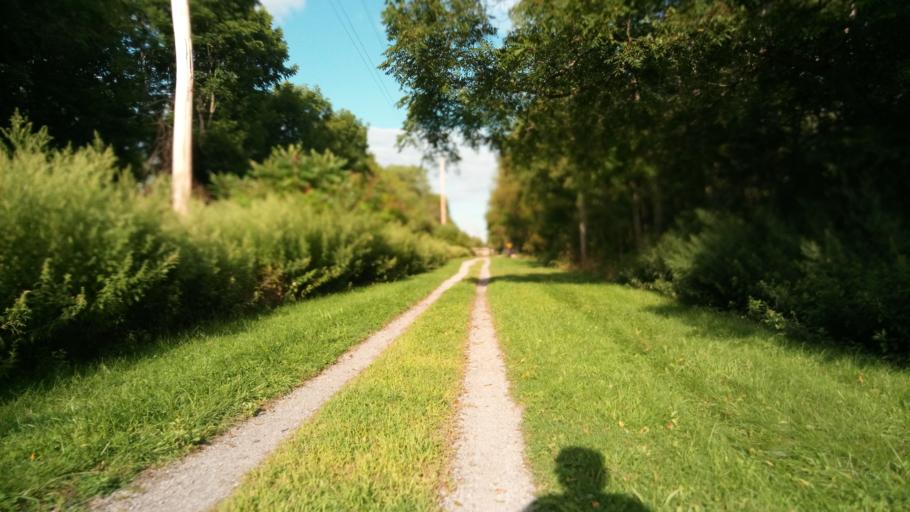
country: US
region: New York
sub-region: Monroe County
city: Pittsford
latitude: 42.9999
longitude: -77.5021
